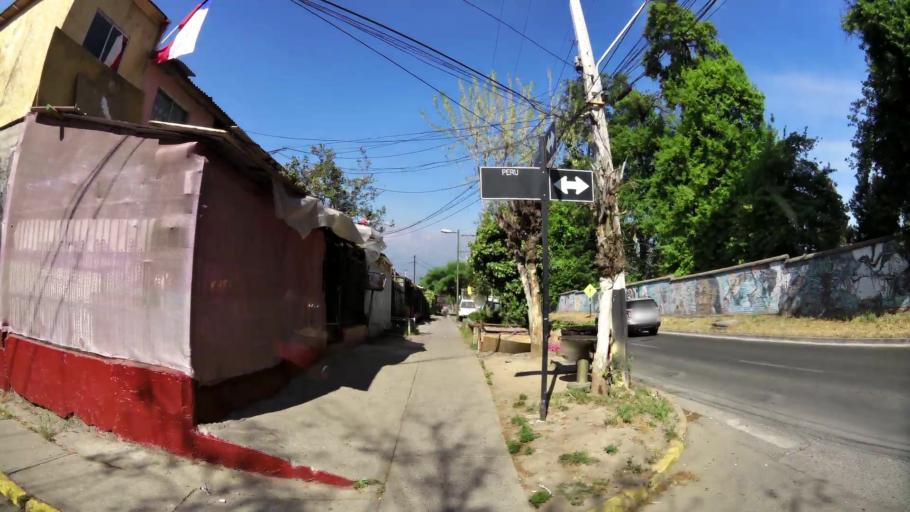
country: CL
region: Santiago Metropolitan
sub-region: Provincia de Santiago
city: Villa Presidente Frei, Nunoa, Santiago, Chile
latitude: -33.4819
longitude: -70.5721
